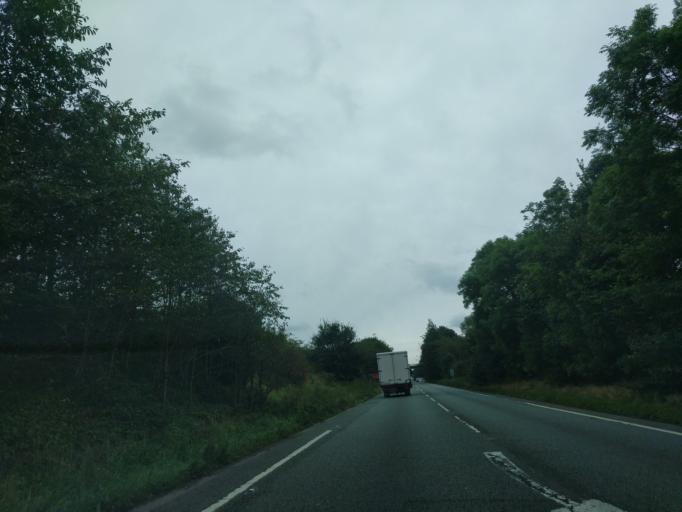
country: GB
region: England
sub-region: Cheshire East
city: Alsager
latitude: 53.0719
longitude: -2.3476
